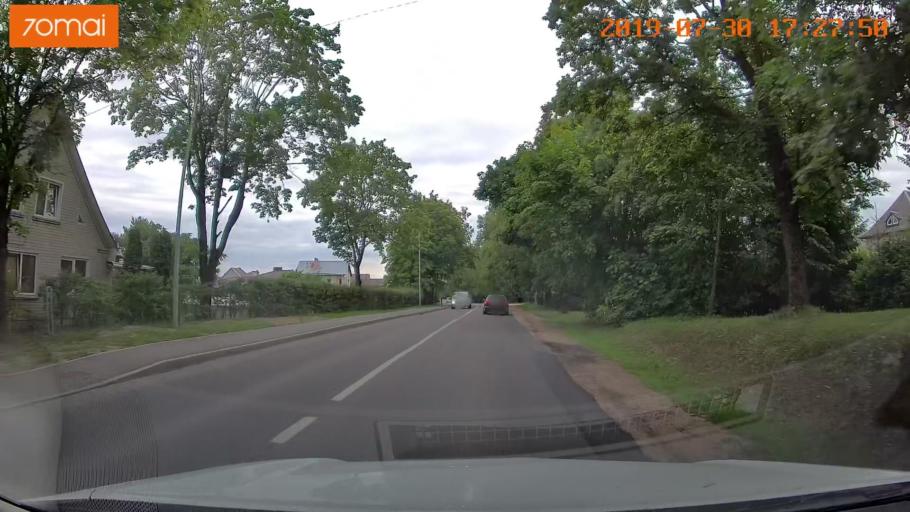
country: LT
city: Skaidiskes
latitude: 54.7102
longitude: 25.4160
